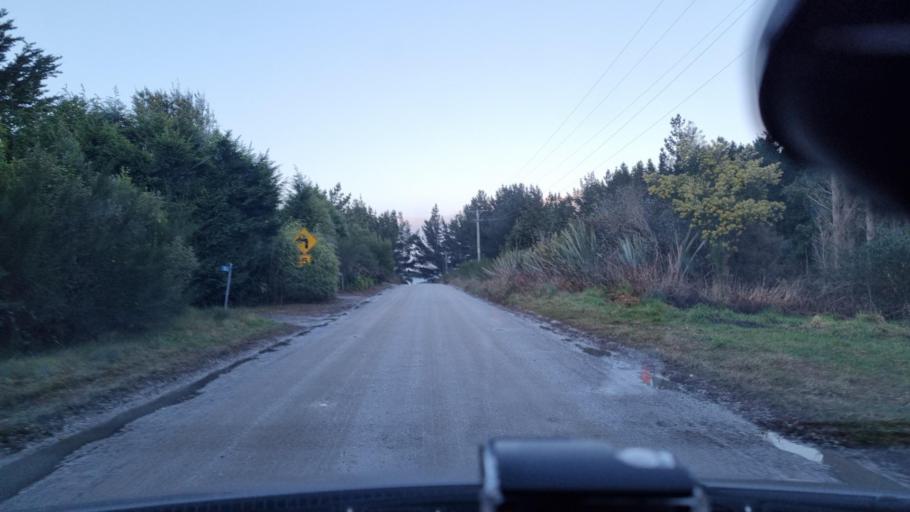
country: NZ
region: Southland
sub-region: Invercargill City
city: Bluff
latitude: -46.5585
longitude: 168.4335
